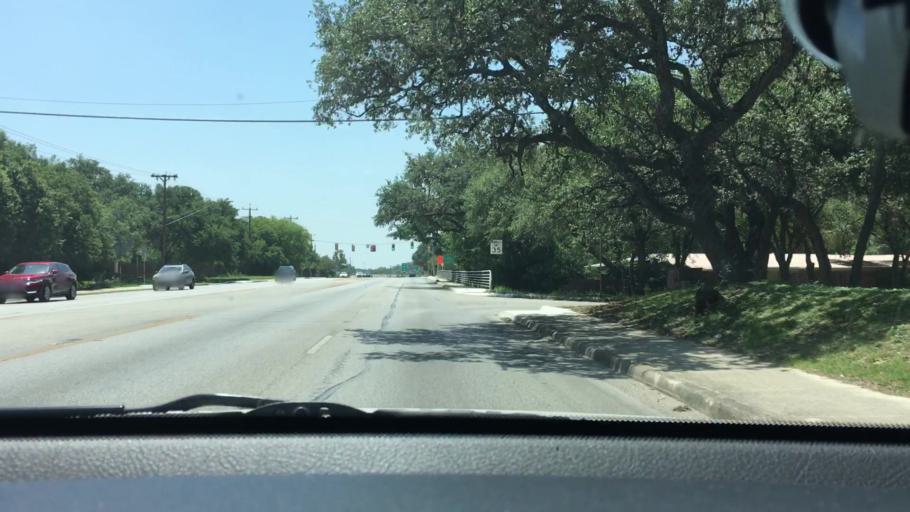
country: US
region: Texas
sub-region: Bexar County
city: Castle Hills
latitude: 29.5258
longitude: -98.5174
